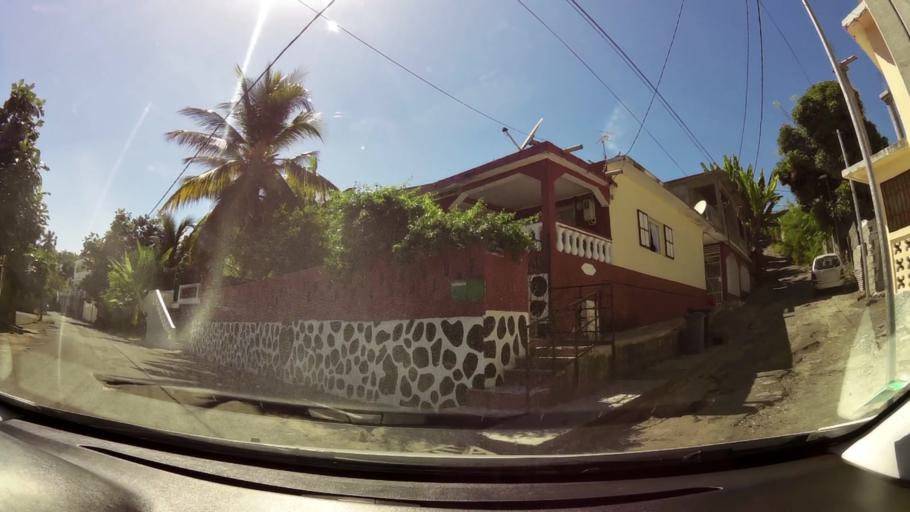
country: YT
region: Pamandzi
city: Pamandzi
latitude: -12.7990
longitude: 45.2808
